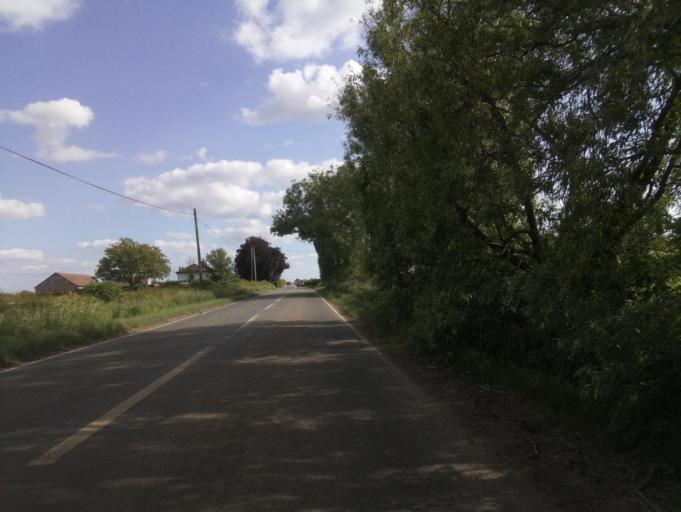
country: GB
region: England
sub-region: Somerset
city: Westonzoyland
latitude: 51.0948
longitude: -2.8773
